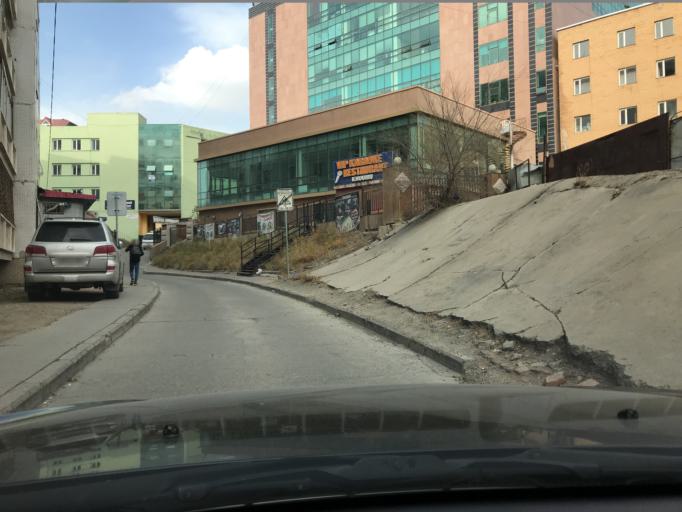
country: MN
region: Ulaanbaatar
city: Ulaanbaatar
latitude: 47.9178
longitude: 106.9415
